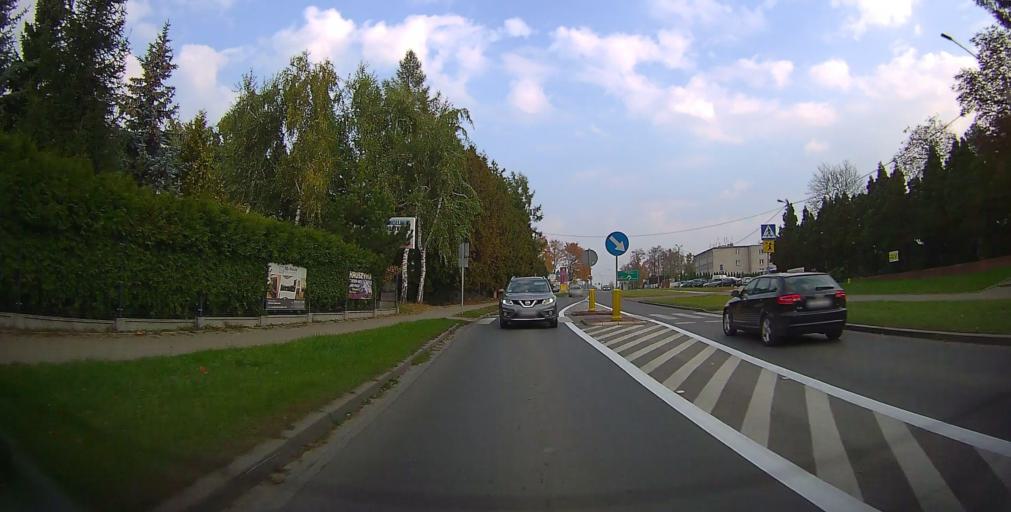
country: PL
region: Masovian Voivodeship
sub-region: Powiat grojecki
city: Belsk Duzy
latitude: 51.8237
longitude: 20.8070
